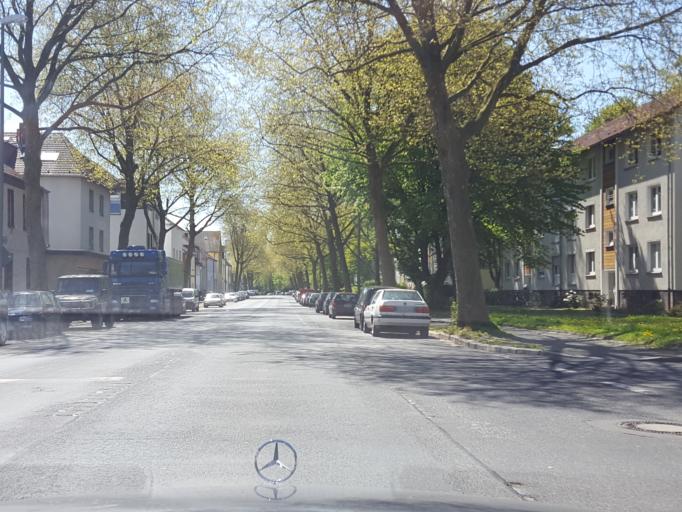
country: DE
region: North Rhine-Westphalia
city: Witten
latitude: 51.4873
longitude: 7.3250
